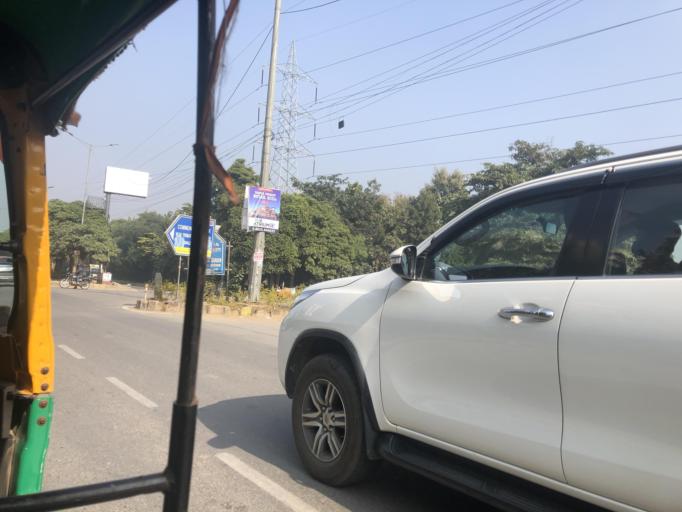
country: IN
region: Haryana
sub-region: Gurgaon
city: Gurgaon
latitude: 28.4321
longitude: 77.0910
